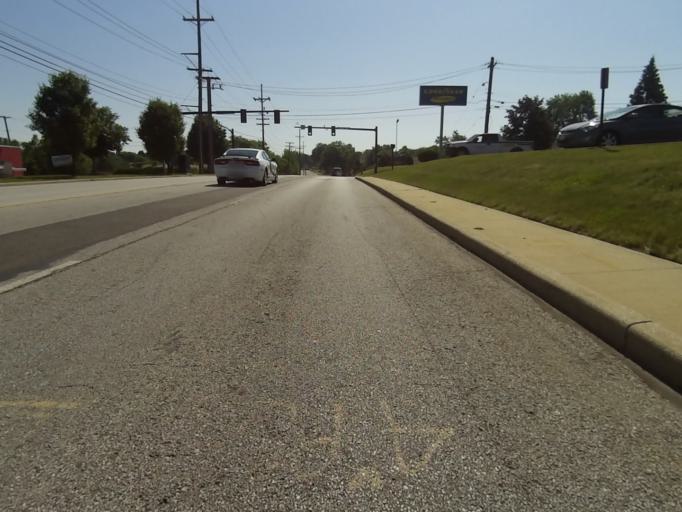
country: US
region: Ohio
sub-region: Summit County
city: Cuyahoga Falls
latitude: 41.1525
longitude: -81.5067
